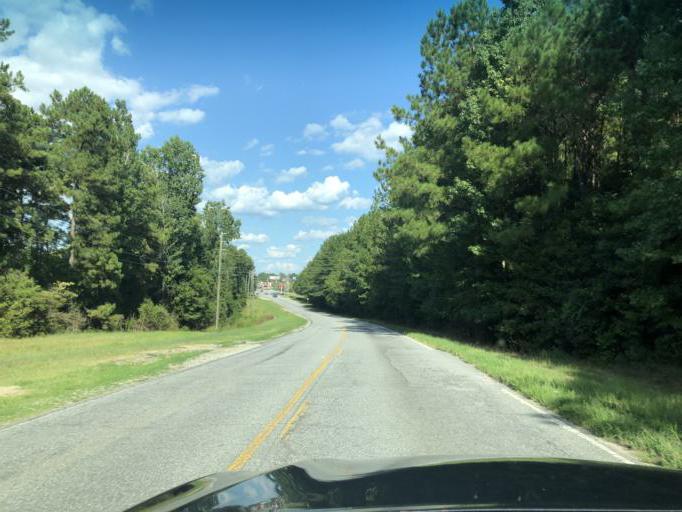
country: US
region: Georgia
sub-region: Muscogee County
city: Columbus
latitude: 32.5203
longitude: -84.8971
